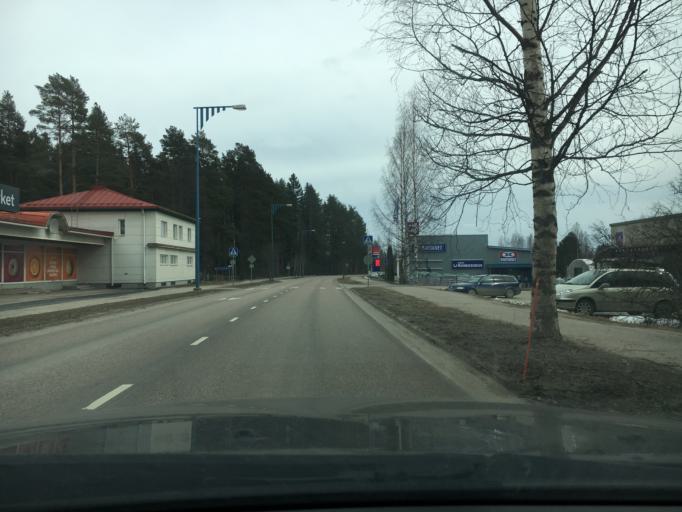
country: FI
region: Central Finland
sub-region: AEaenekoski
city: Konnevesi
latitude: 62.6279
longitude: 26.2922
